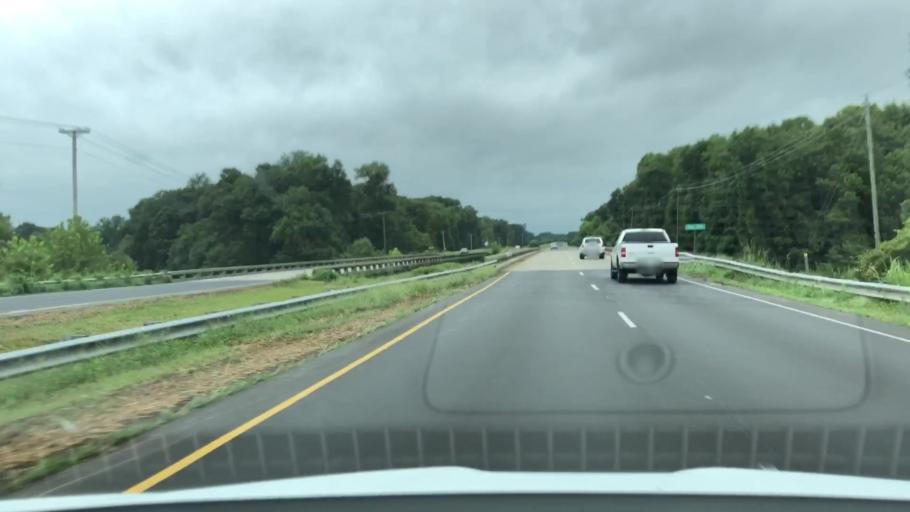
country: US
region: North Carolina
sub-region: Lenoir County
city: Kinston
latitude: 35.2608
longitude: -77.6180
